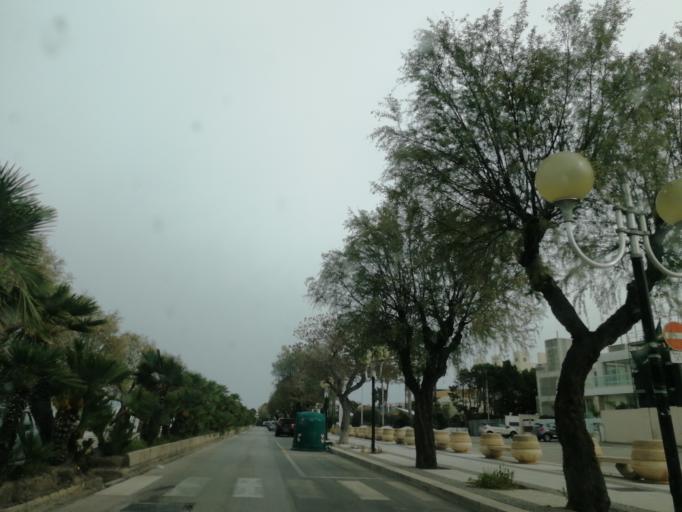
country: IT
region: Apulia
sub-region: Provincia di Barletta - Andria - Trani
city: Barletta
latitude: 41.3214
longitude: 16.2947
